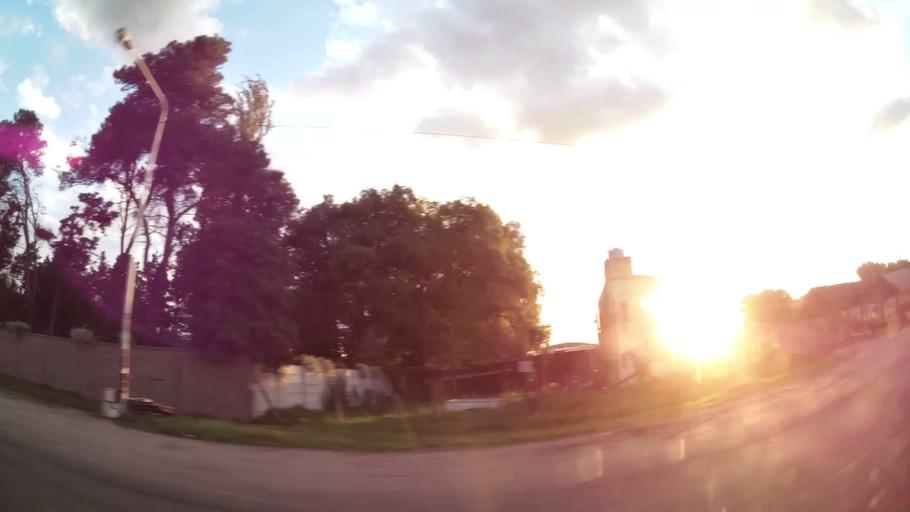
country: AR
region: Buenos Aires
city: Santa Catalina - Dique Lujan
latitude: -34.4929
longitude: -58.7645
